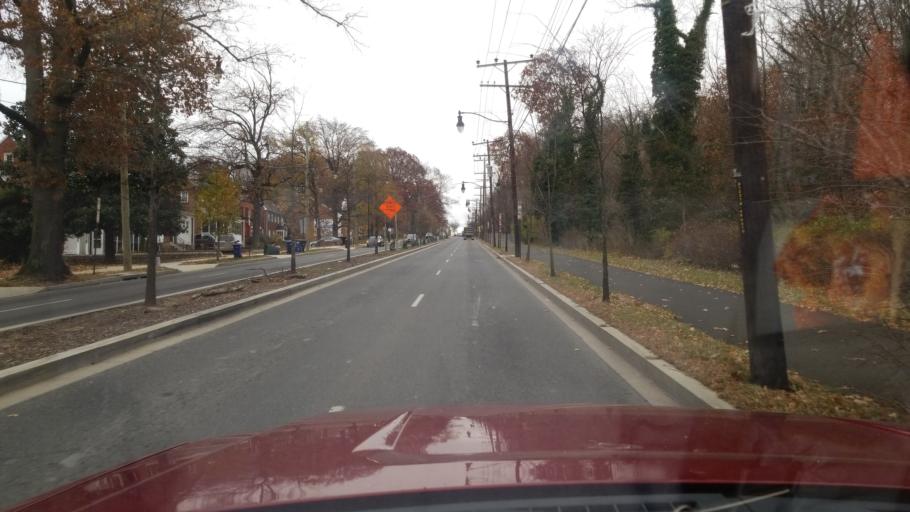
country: US
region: Maryland
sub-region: Prince George's County
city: Silver Hill
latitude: 38.8673
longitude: -76.9557
